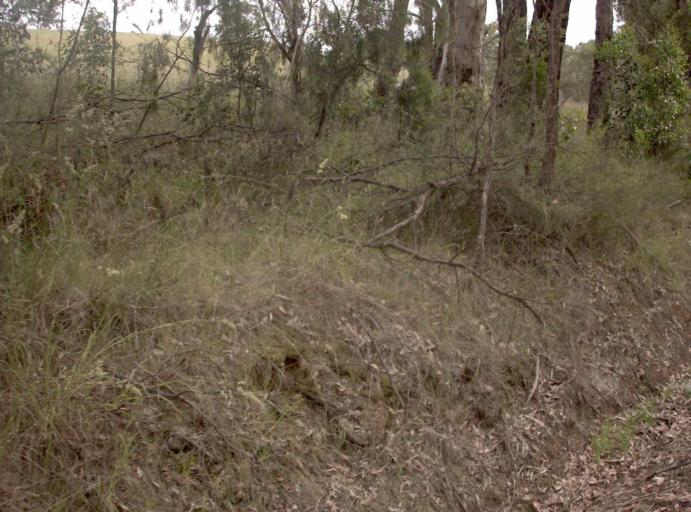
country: AU
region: Victoria
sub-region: East Gippsland
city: Bairnsdale
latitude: -37.7210
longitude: 147.5919
